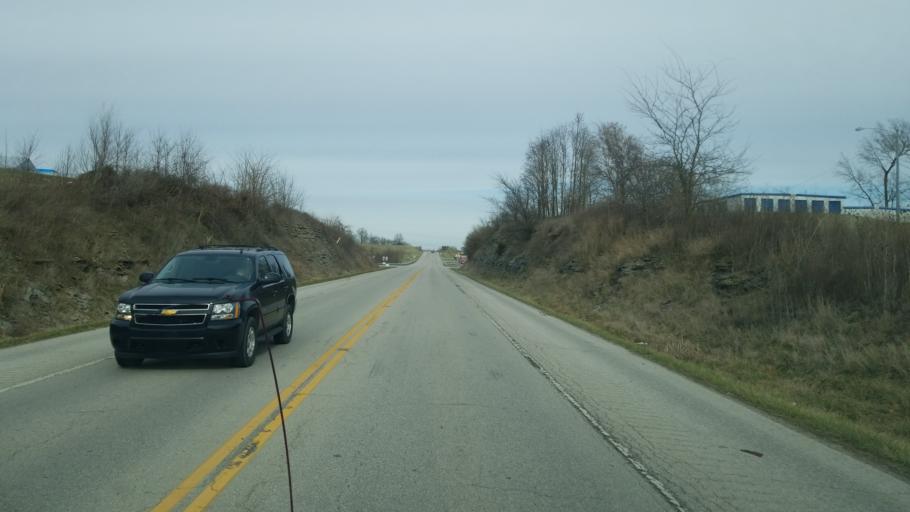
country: US
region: Kentucky
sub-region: Fleming County
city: Flemingsburg
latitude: 38.5222
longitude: -83.8355
